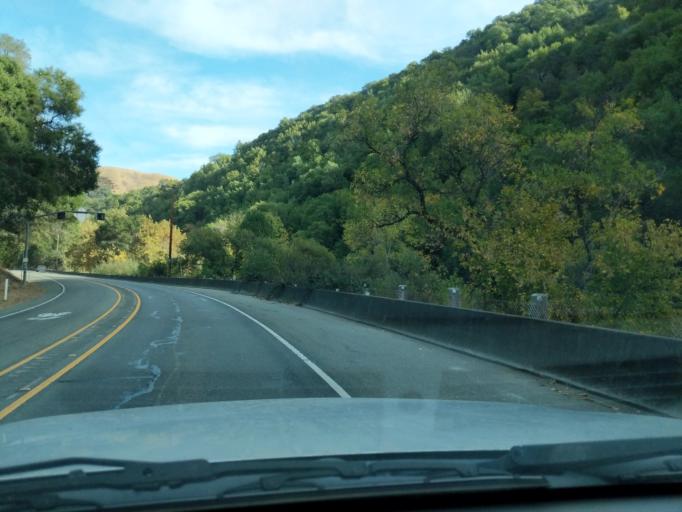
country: US
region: California
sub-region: Alameda County
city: Fremont
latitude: 37.5975
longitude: -121.9461
